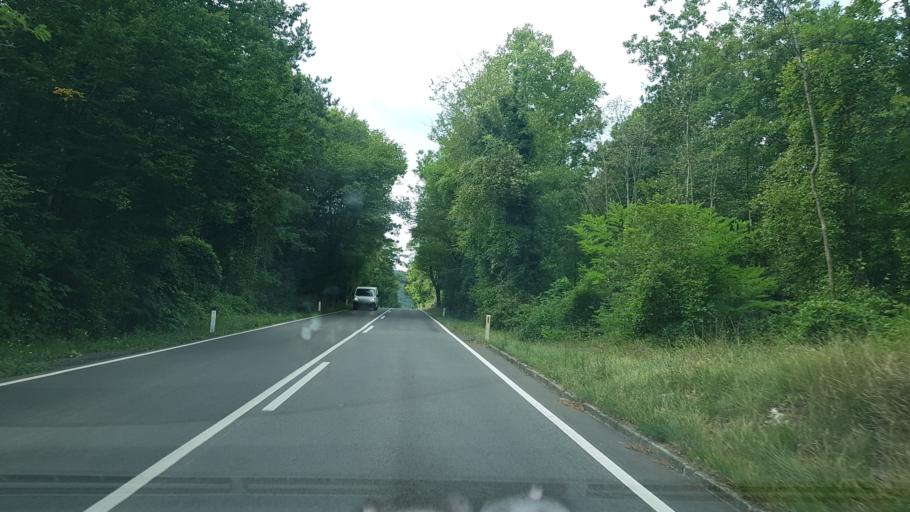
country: SI
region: Divaca
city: Divaca
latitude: 45.6710
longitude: 13.9481
